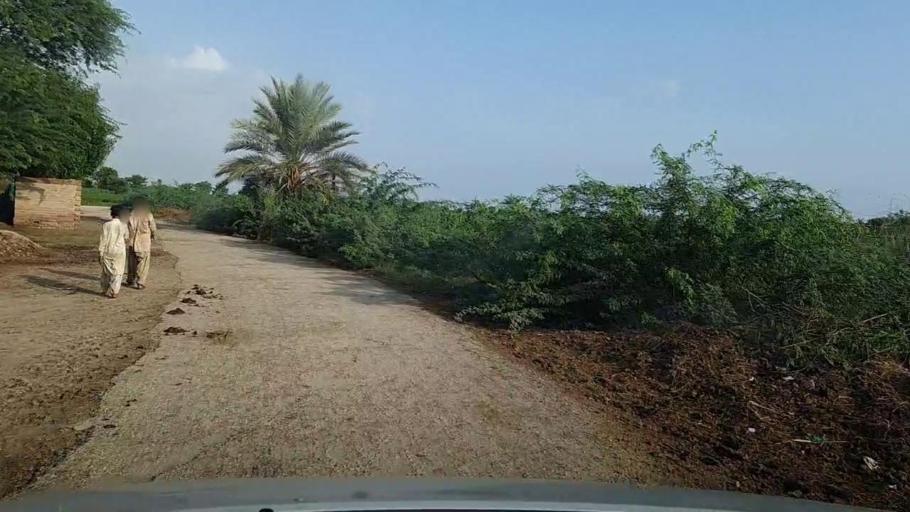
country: PK
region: Sindh
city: Pad Idan
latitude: 26.8074
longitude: 68.2353
